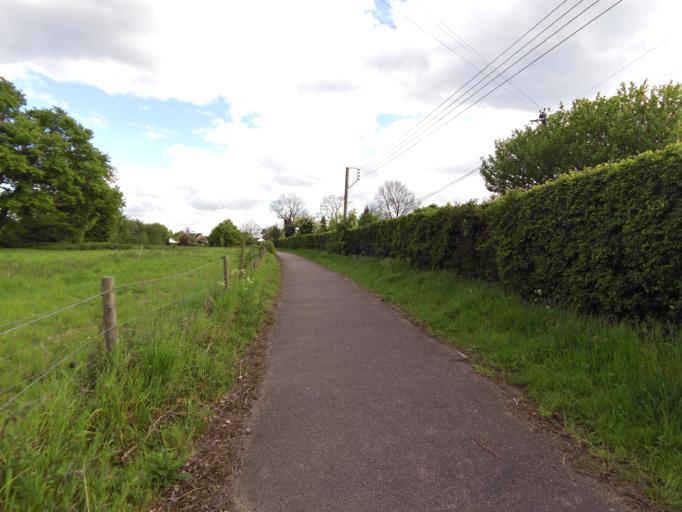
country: GB
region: England
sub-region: Suffolk
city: Woolpit
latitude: 52.2176
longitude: 0.9007
